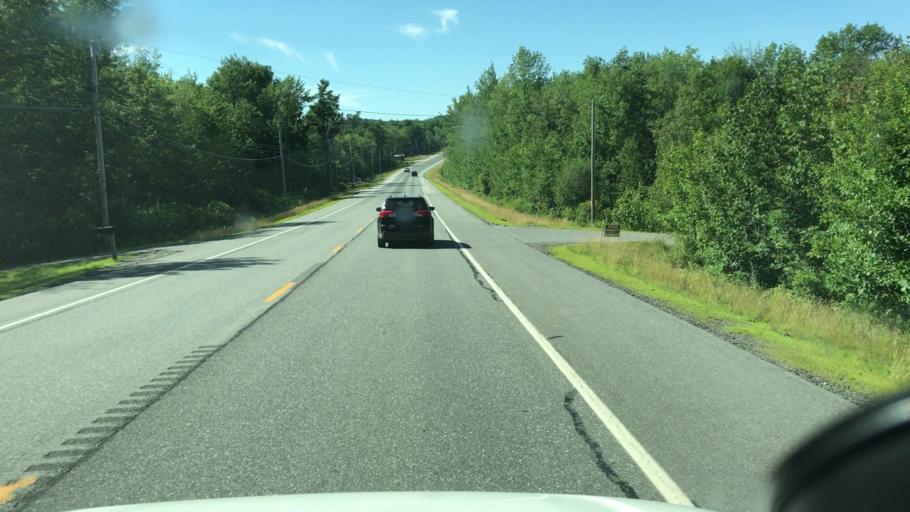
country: US
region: Maine
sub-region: Hancock County
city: Dedham
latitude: 44.6311
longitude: -68.5415
